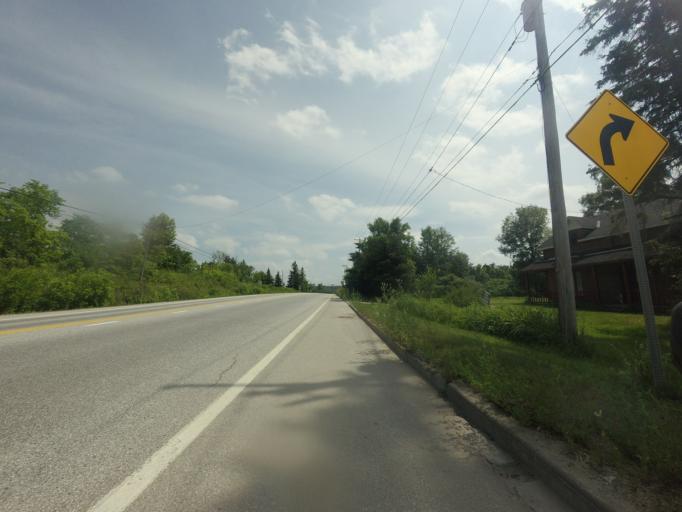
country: CA
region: Quebec
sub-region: Outaouais
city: Wakefield
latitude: 45.8017
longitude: -75.9456
